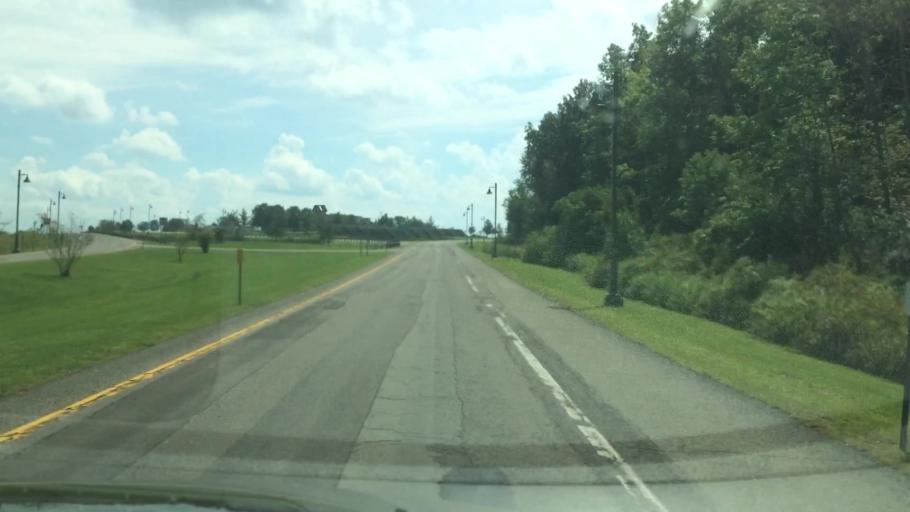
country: US
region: New York
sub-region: Chautauqua County
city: Lakewood
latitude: 42.1375
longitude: -79.3513
